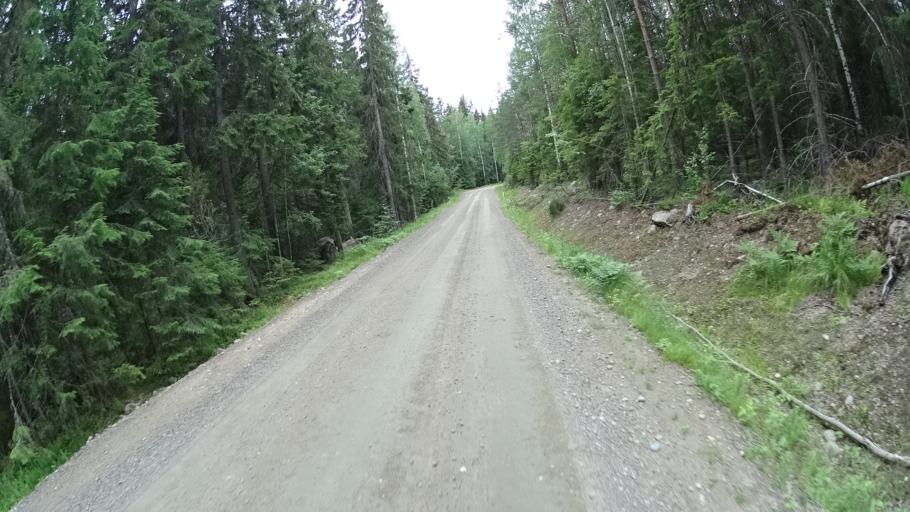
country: FI
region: Southern Savonia
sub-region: Mikkeli
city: Maentyharju
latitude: 61.1543
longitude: 26.8918
